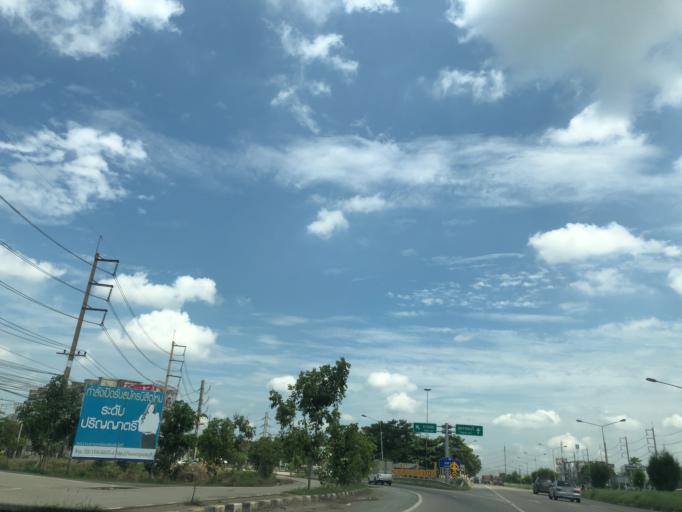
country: TH
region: Pathum Thani
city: Lat Lum Kaeo
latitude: 14.0274
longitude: 100.3538
